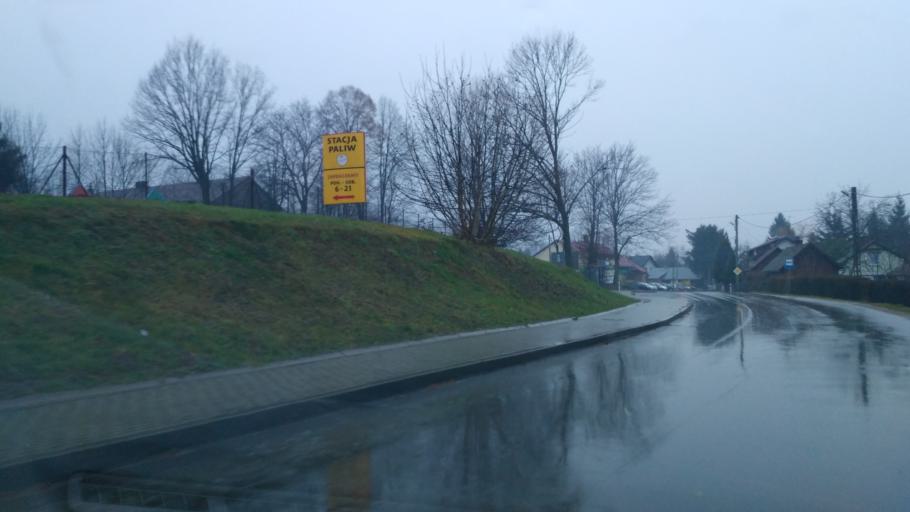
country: PL
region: Subcarpathian Voivodeship
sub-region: Powiat lancucki
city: Krzemienica
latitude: 50.0732
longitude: 22.1894
